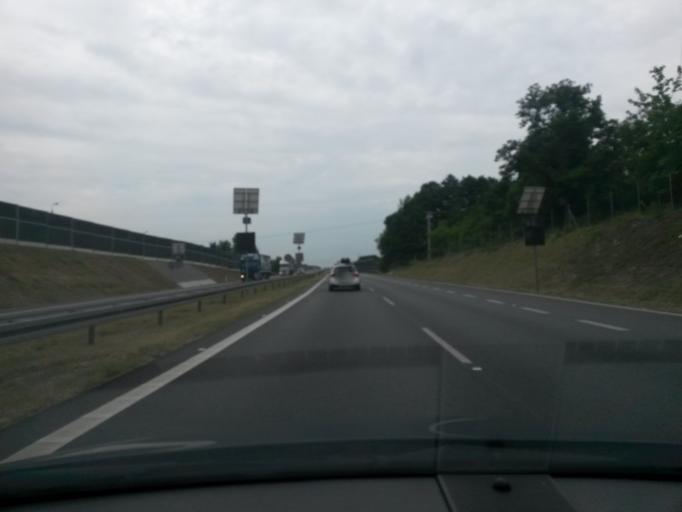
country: PL
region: Masovian Voivodeship
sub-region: Powiat zyrardowski
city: Mszczonow
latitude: 51.9738
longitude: 20.5038
